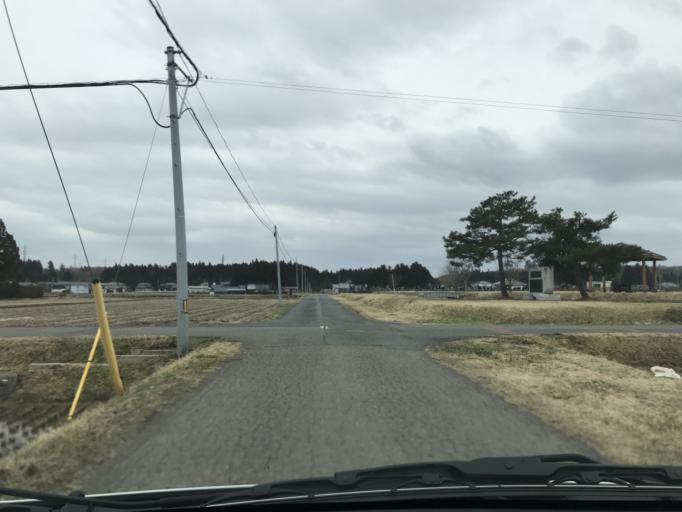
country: JP
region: Iwate
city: Kitakami
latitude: 39.2232
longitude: 141.0768
